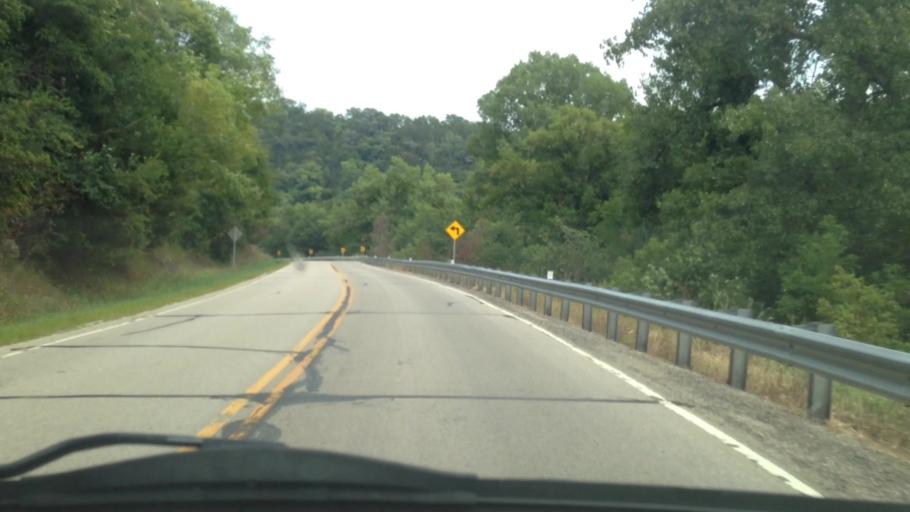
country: US
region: Minnesota
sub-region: Fillmore County
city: Preston
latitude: 43.7230
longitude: -91.9655
